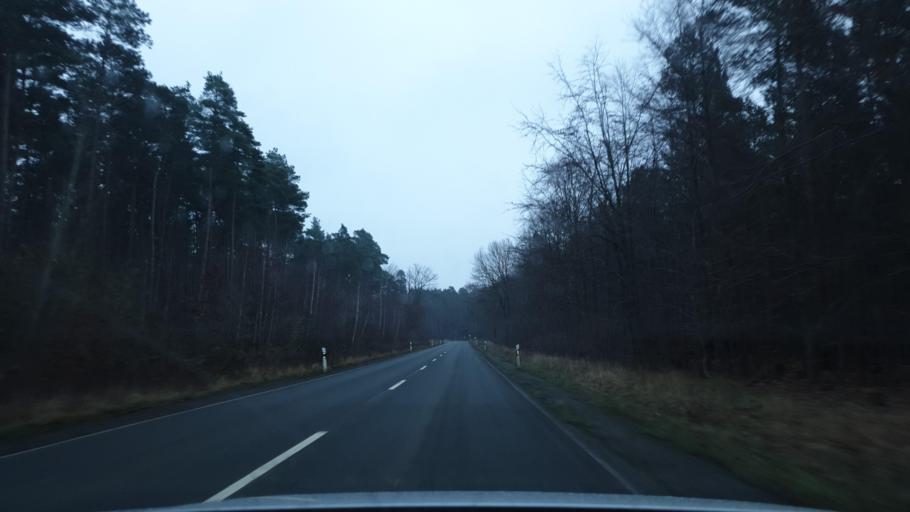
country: DE
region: North Rhine-Westphalia
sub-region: Regierungsbezirk Detmold
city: Petershagen
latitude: 52.3653
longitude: 8.9096
